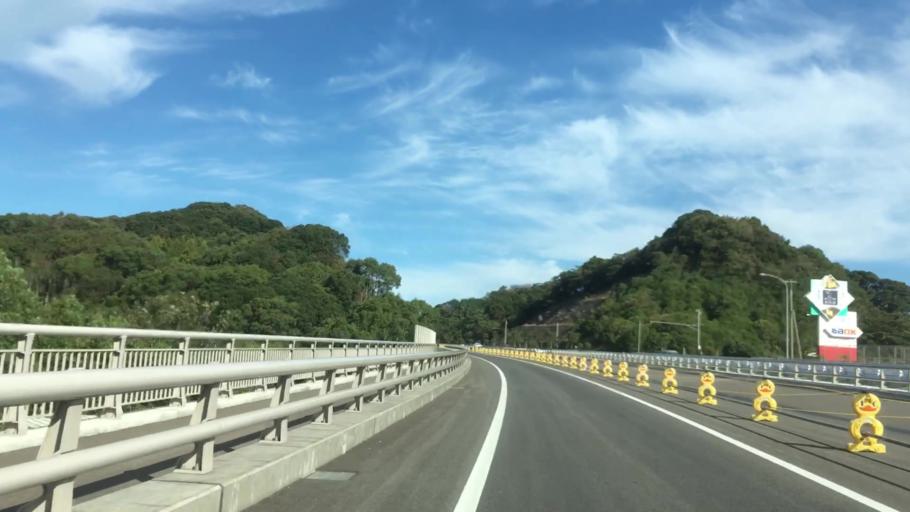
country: JP
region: Nagasaki
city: Sasebo
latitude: 33.1190
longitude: 129.7925
